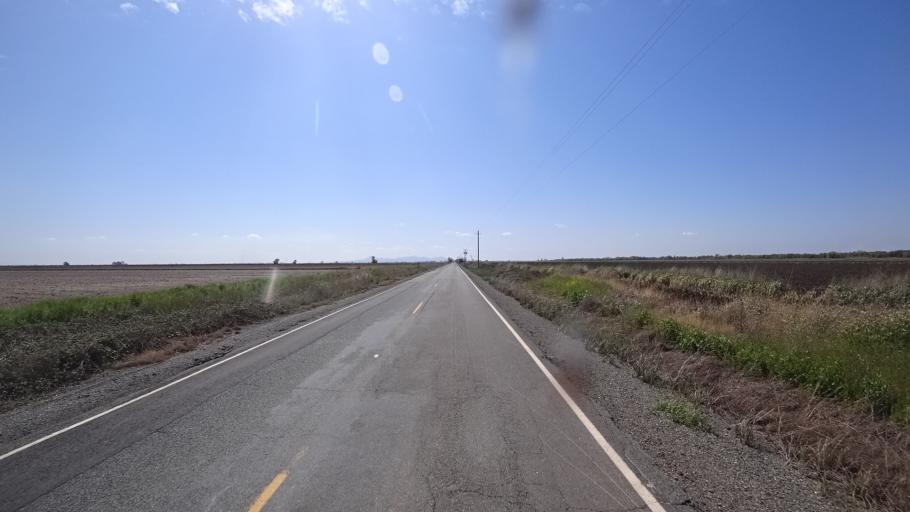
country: US
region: California
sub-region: Butte County
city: Biggs
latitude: 39.4845
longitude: -121.8575
